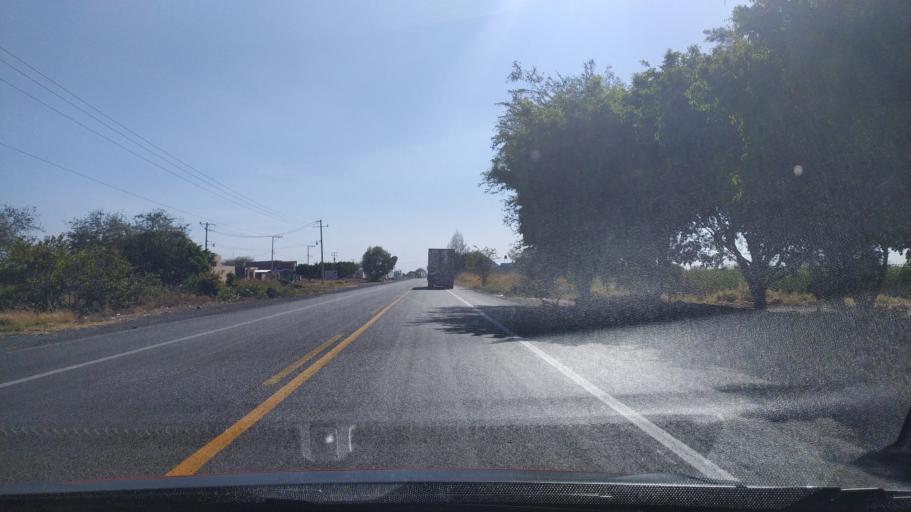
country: MX
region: Michoacan
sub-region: Yurecuaro
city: Yurecuaro
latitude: 20.3256
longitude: -102.2747
